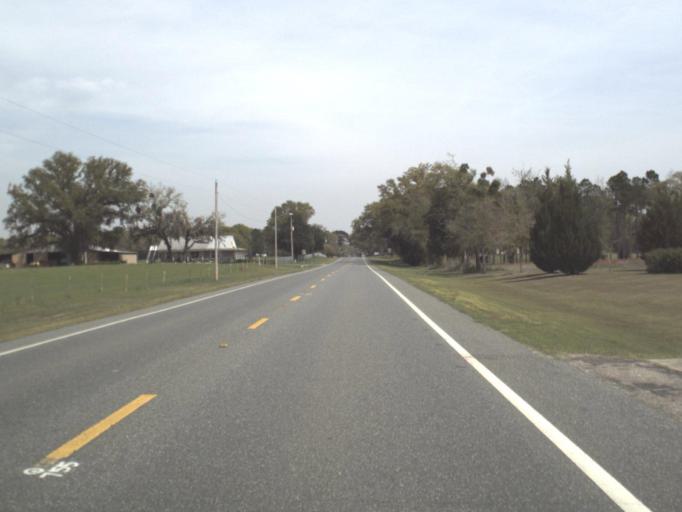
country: US
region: Florida
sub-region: Jackson County
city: Malone
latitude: 30.9583
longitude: -85.1748
